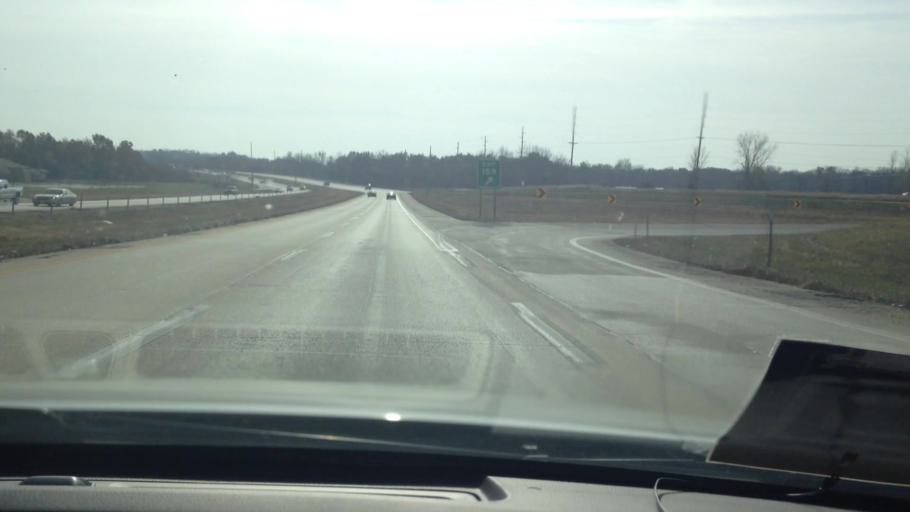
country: US
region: Missouri
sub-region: Cass County
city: Harrisonville
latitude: 38.6522
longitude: -94.3658
